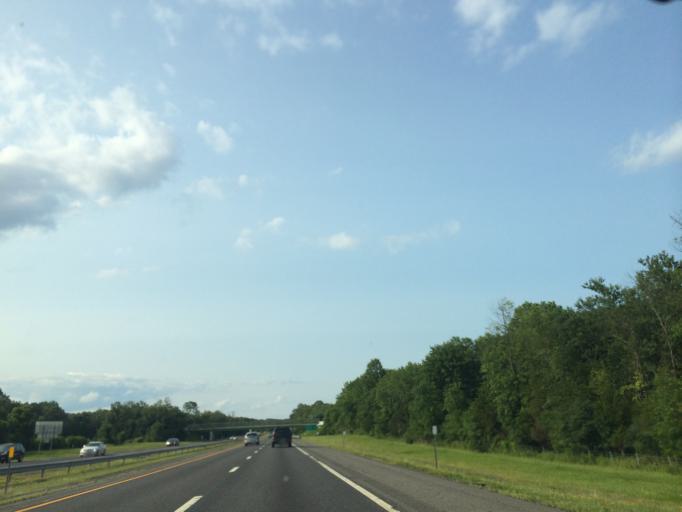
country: US
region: New York
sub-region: Ulster County
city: Saugerties
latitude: 42.1183
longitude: -73.9560
